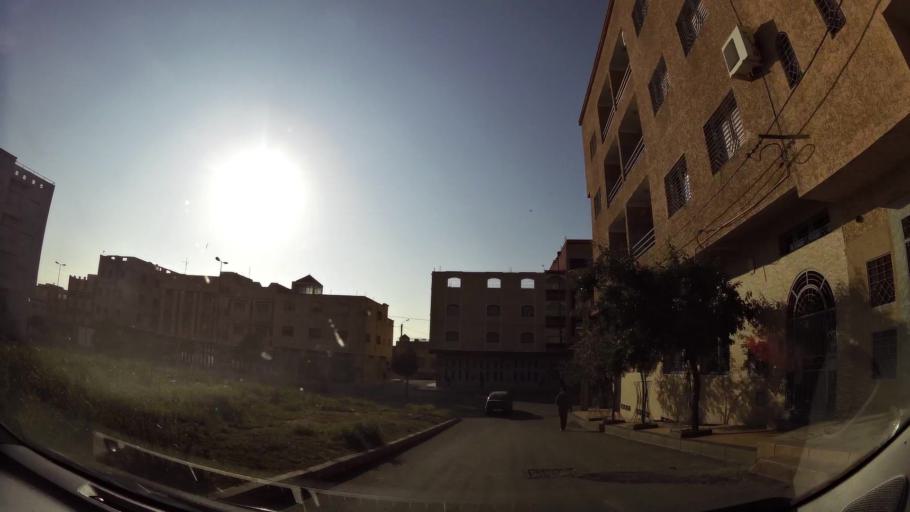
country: MA
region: Oriental
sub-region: Oujda-Angad
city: Oujda
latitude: 34.6776
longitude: -1.9377
